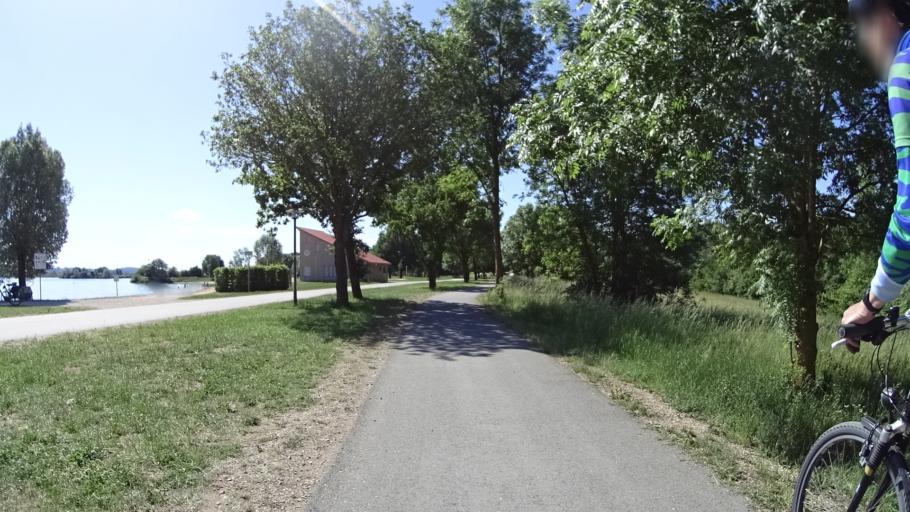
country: DE
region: Bavaria
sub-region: Regierungsbezirk Mittelfranken
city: Muhr am See
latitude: 49.1248
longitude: 10.7208
